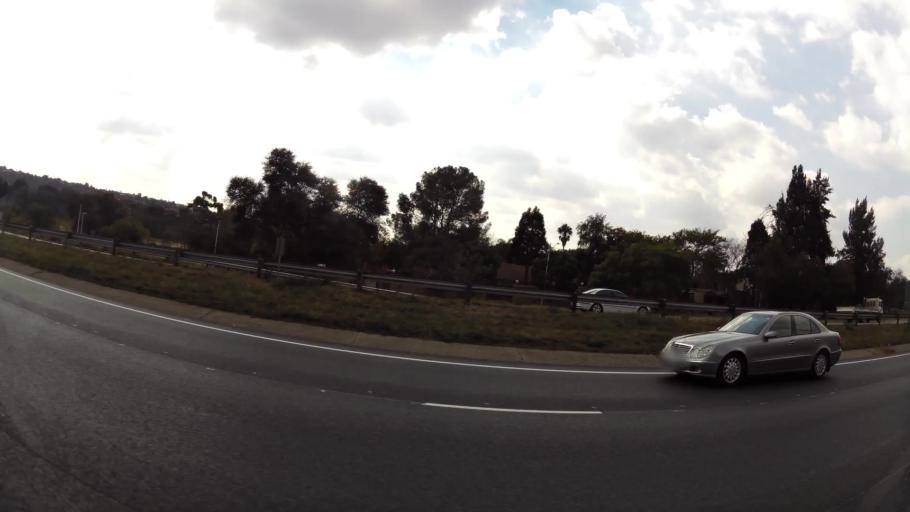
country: ZA
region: Gauteng
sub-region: City of Tshwane Metropolitan Municipality
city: Pretoria
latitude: -25.7513
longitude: 28.2977
